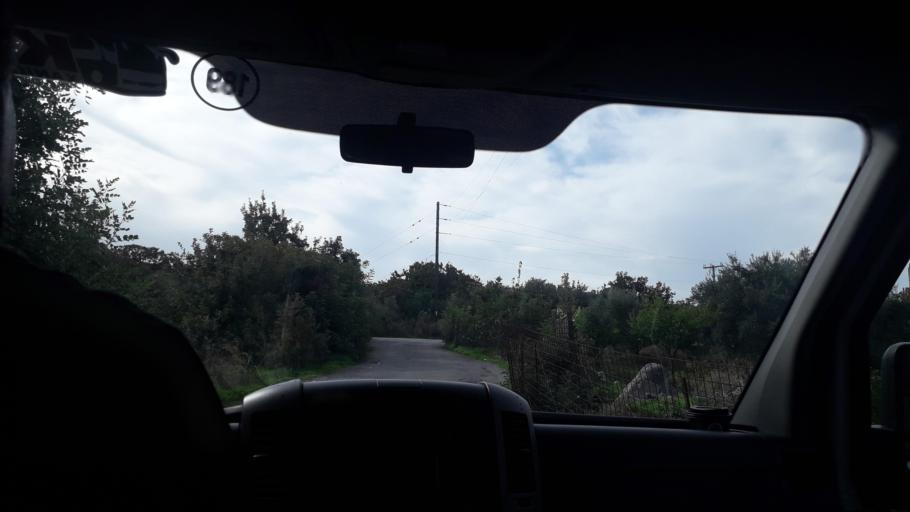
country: GR
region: Crete
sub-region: Nomos Rethymnis
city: Atsipopoulon
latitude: 35.3585
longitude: 24.4322
